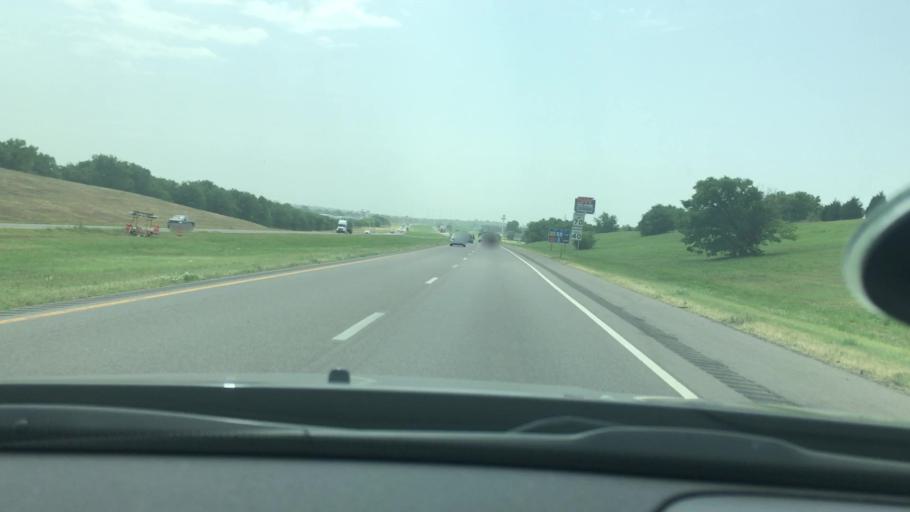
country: US
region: Oklahoma
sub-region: Garvin County
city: Pauls Valley
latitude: 34.7532
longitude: -97.2774
